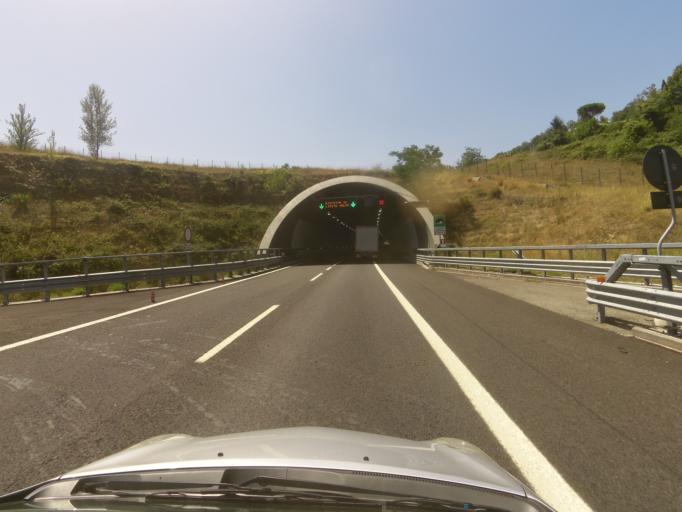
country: IT
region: Tuscany
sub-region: Province of Florence
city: Barberino di Mugello
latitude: 44.0429
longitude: 11.2350
